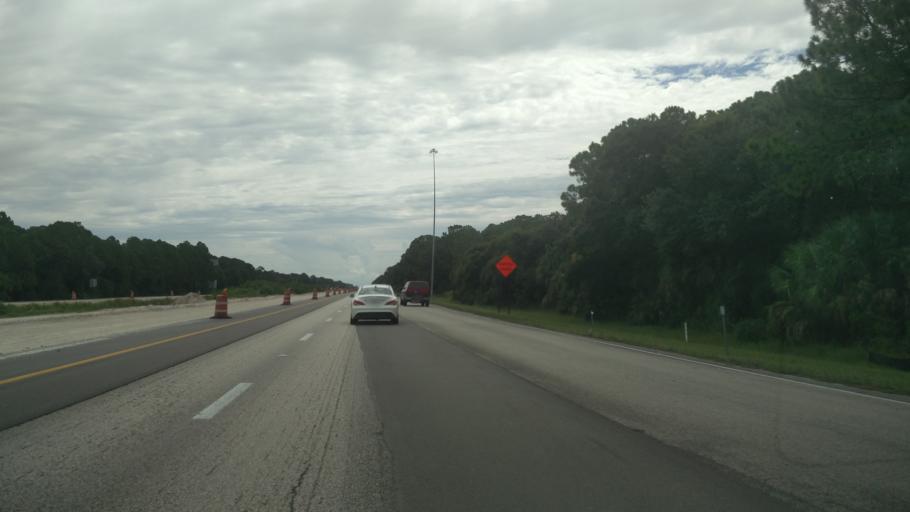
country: US
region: Florida
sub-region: Sarasota County
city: North Port
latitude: 27.0990
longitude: -82.1985
